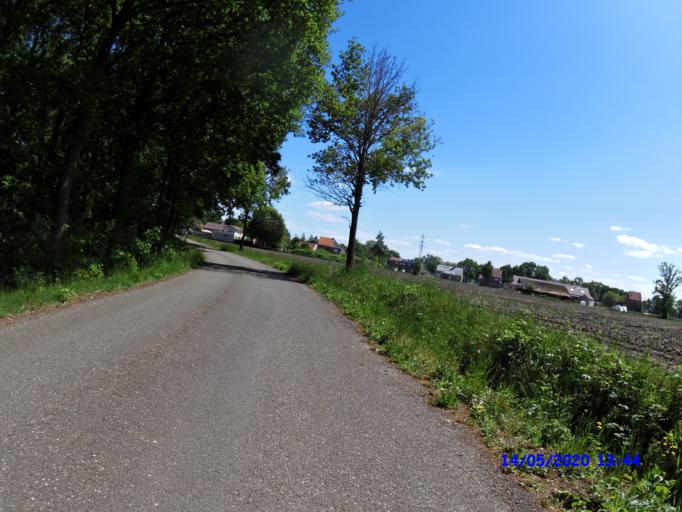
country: BE
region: Flanders
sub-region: Provincie Antwerpen
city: Geel
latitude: 51.1770
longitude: 5.0104
